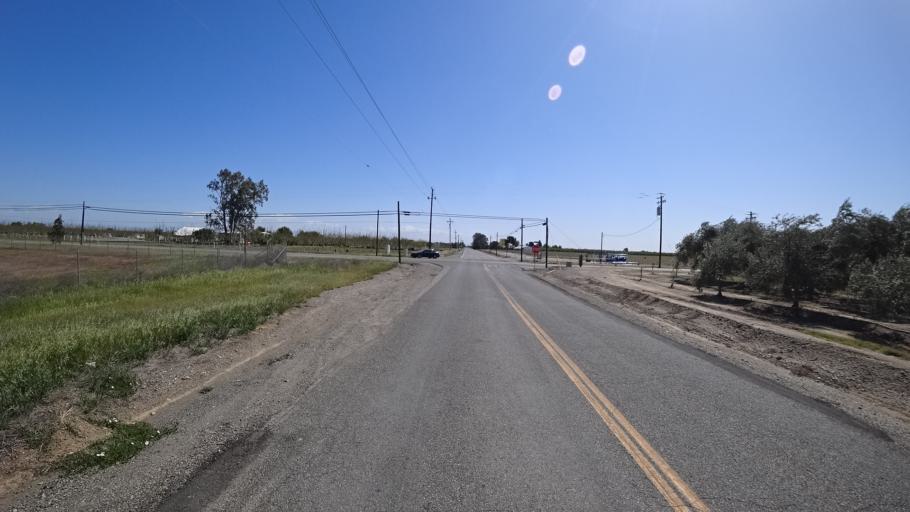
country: US
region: California
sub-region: Glenn County
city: Orland
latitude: 39.7107
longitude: -122.1416
